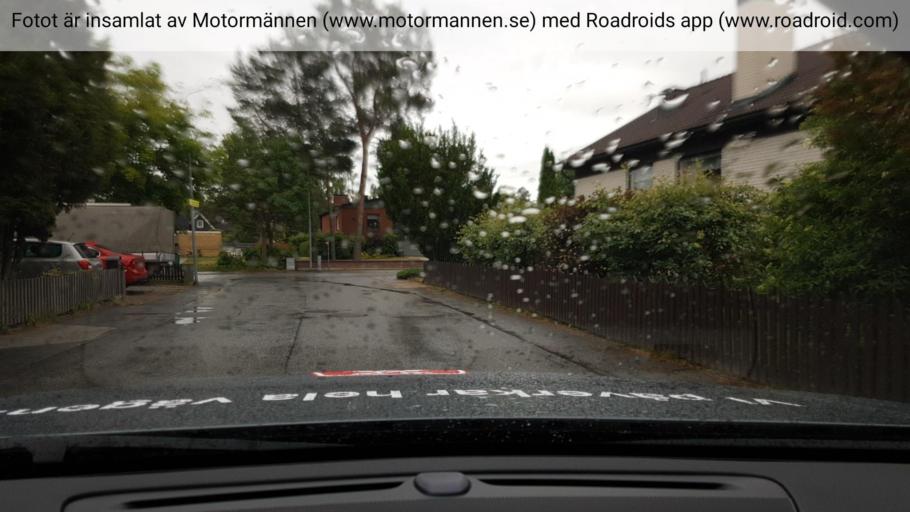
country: SE
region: Stockholm
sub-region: Vallentuna Kommun
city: Vallentuna
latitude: 59.5163
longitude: 18.0644
